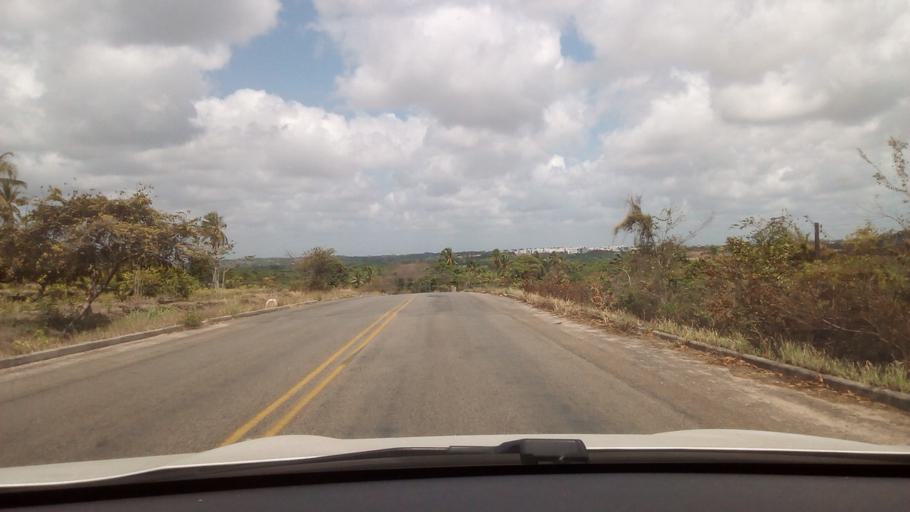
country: BR
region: Paraiba
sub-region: Conde
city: Conde
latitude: -7.2418
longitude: -34.8338
